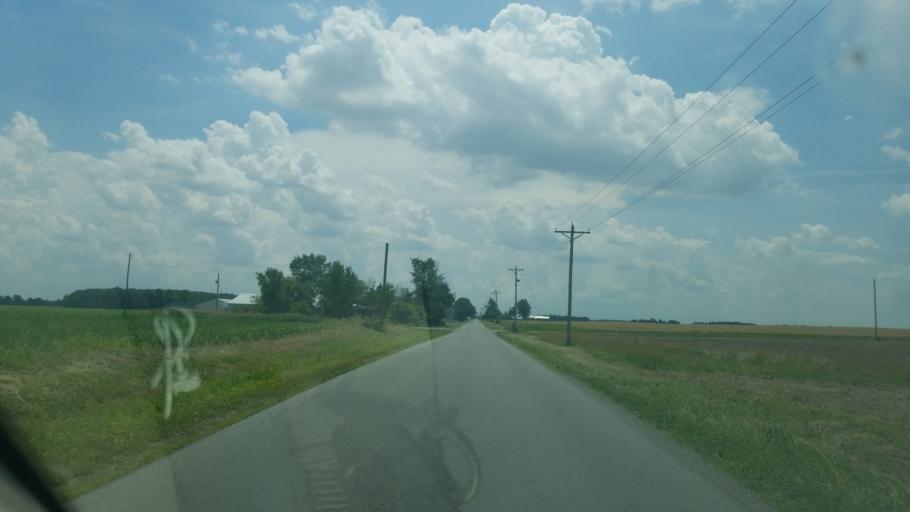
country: US
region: Ohio
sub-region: Hancock County
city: Arlington
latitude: 40.8499
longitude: -83.5998
